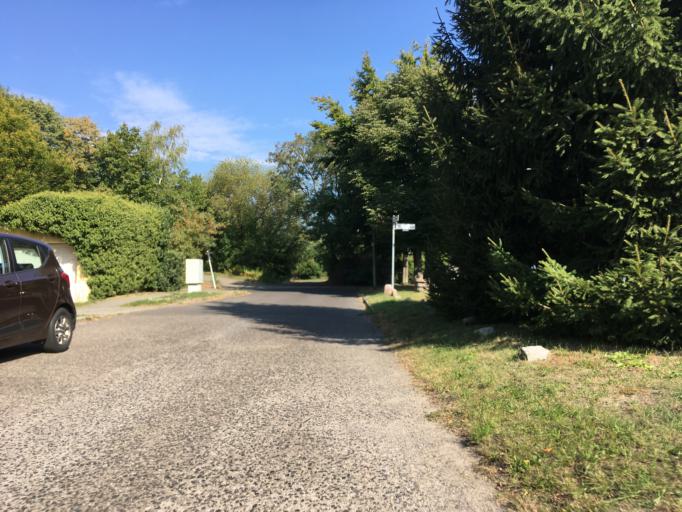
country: DE
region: Berlin
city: Biesdorf
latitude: 52.5125
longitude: 13.5456
